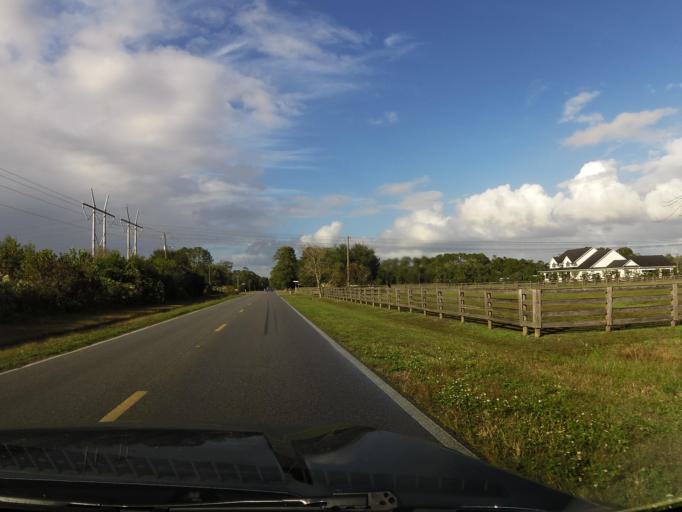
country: US
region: Florida
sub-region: Clay County
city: Asbury Lake
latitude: 30.0288
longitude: -81.8467
